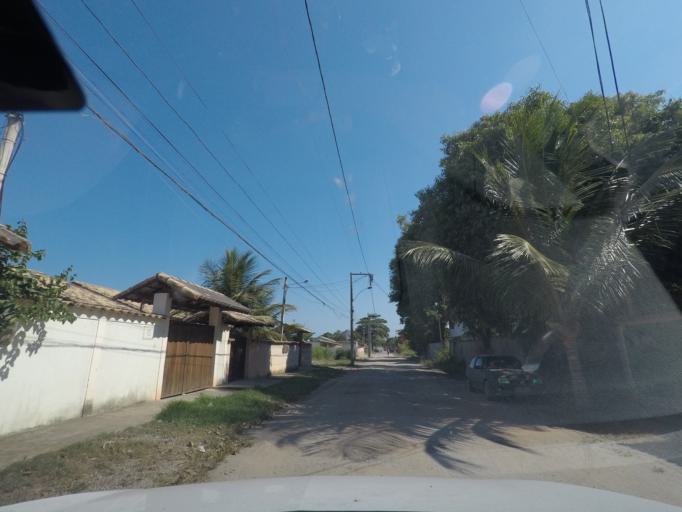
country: BR
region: Rio de Janeiro
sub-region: Niteroi
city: Niteroi
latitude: -22.9590
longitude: -42.9730
